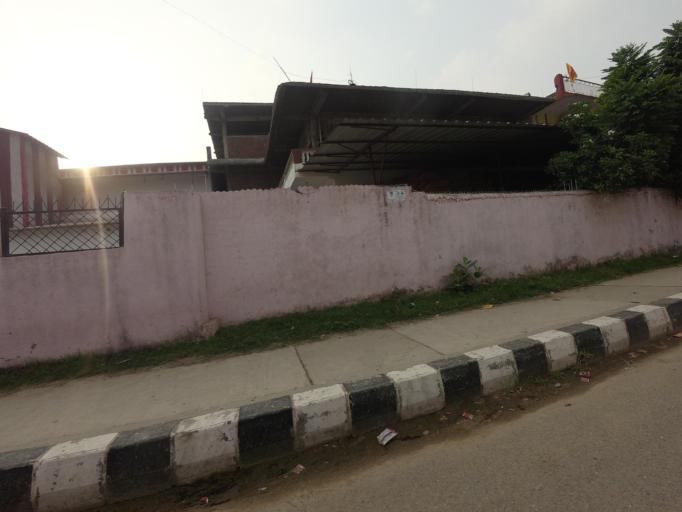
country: NP
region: Western Region
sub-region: Lumbini Zone
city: Bhairahawa
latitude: 27.5067
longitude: 83.4415
